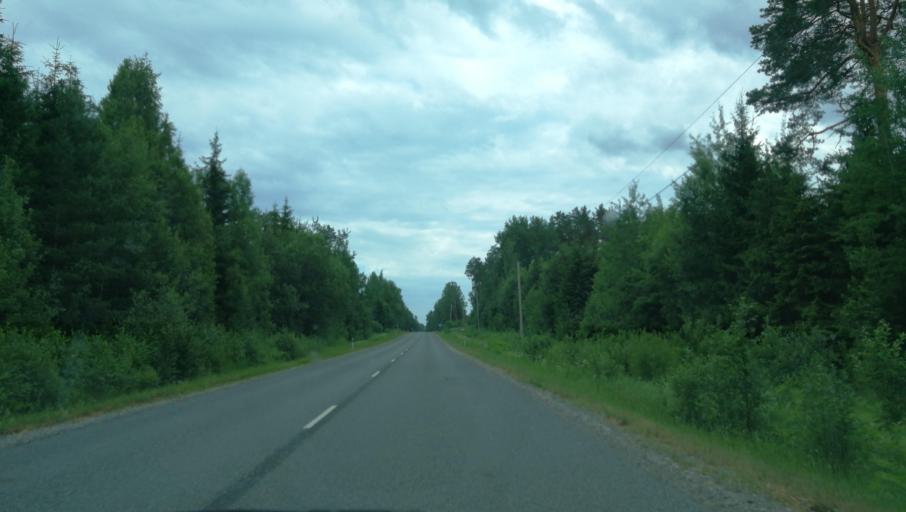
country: LV
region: Naukseni
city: Naukseni
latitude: 57.7247
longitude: 25.4222
